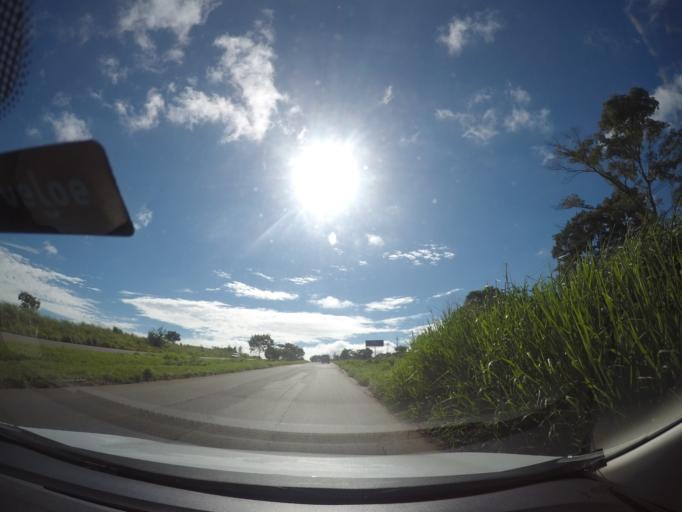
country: BR
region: Goias
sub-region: Senador Canedo
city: Senador Canedo
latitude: -16.6506
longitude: -49.1640
